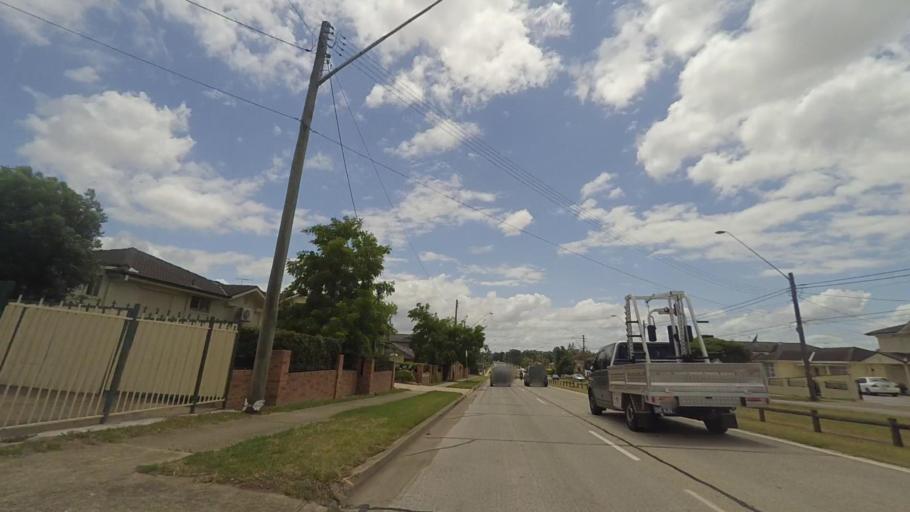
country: AU
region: New South Wales
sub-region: Fairfield
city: Cabramatta West
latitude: -33.8807
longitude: 150.9243
